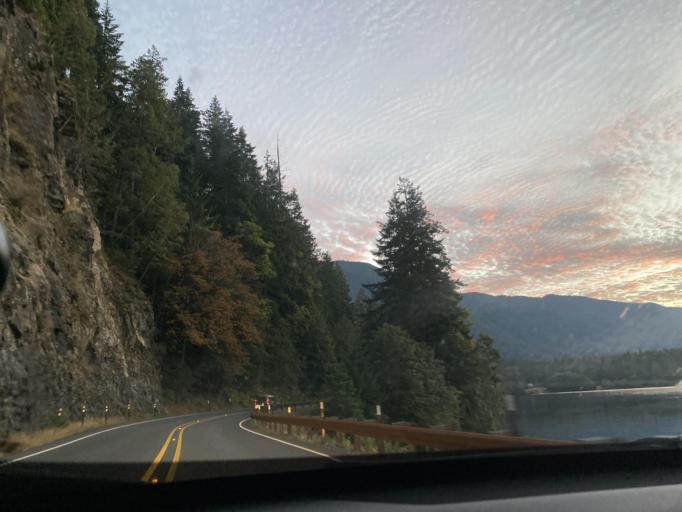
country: CA
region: British Columbia
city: Sooke
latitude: 48.0630
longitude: -123.7767
